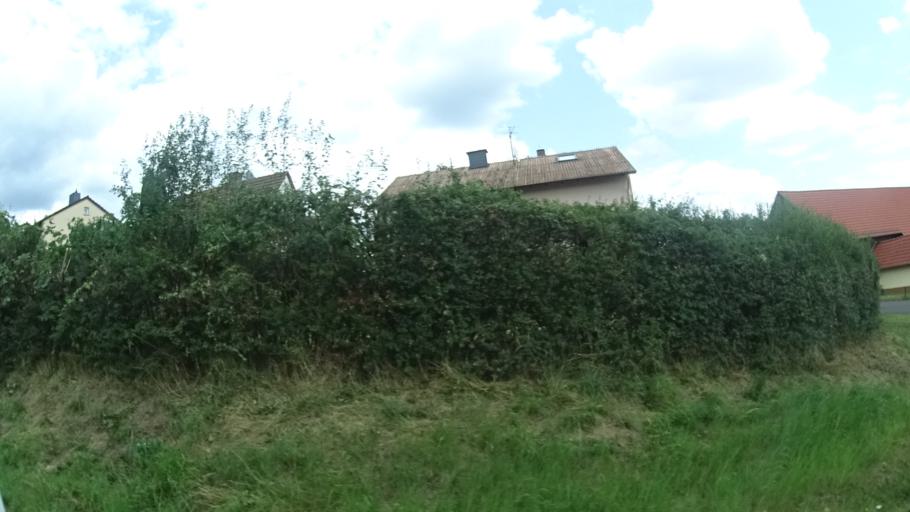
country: DE
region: Hesse
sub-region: Regierungsbezirk Darmstadt
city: Kefenrod
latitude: 50.3871
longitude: 9.1964
